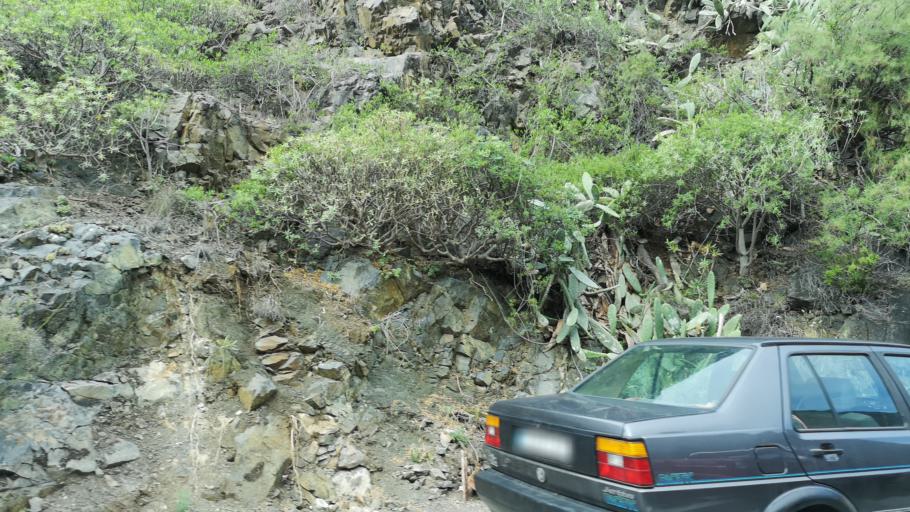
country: ES
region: Canary Islands
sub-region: Provincia de Santa Cruz de Tenerife
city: Vallehermosa
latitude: 28.1967
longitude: -17.2571
